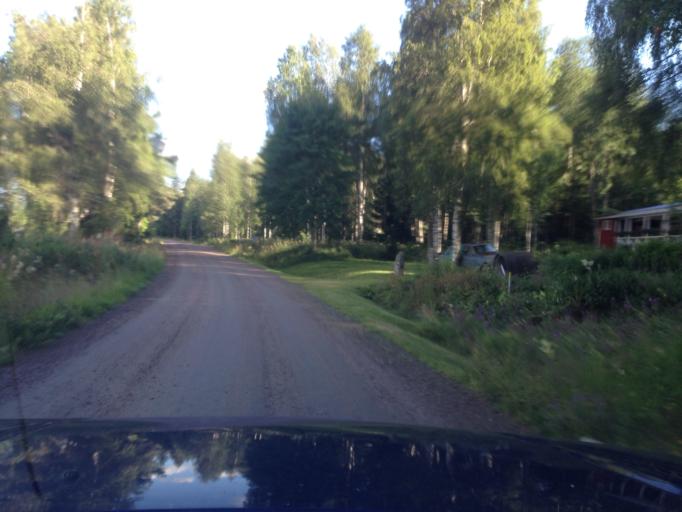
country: SE
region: Dalarna
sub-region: Ludvika Kommun
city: Abborrberget
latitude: 60.2700
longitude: 14.7316
